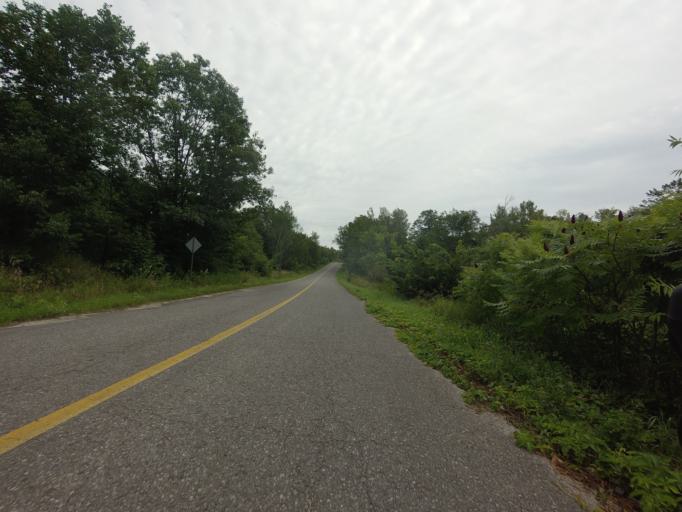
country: CA
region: Ontario
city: Perth
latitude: 44.6762
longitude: -76.6558
